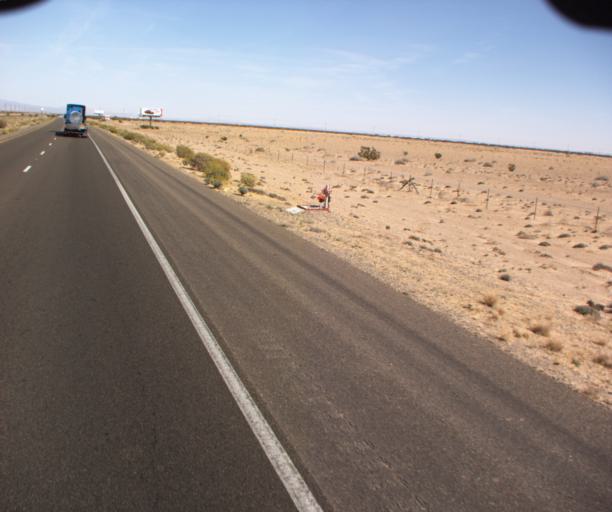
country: MX
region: Sonora
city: San Luis Rio Colorado
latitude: 32.4945
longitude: -114.6910
